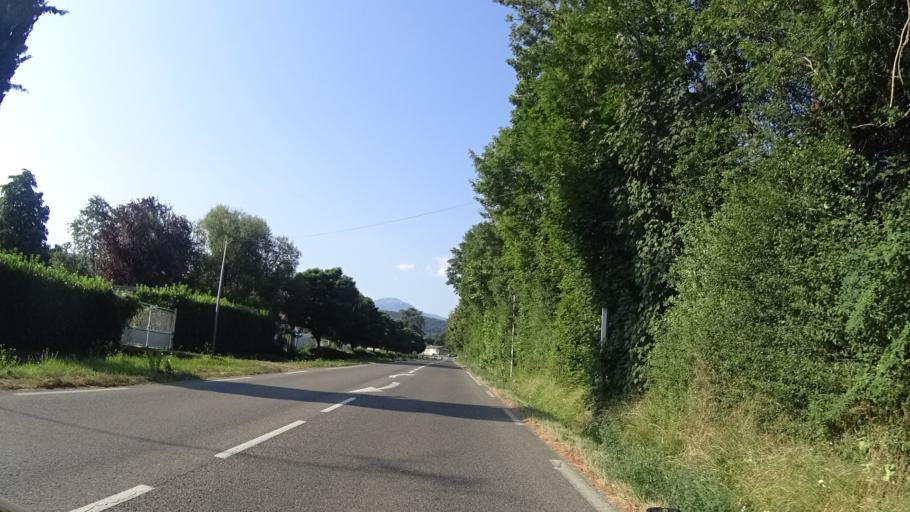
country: FR
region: Midi-Pyrenees
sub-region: Departement de l'Ariege
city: Lavelanet
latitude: 42.9527
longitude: 1.8602
